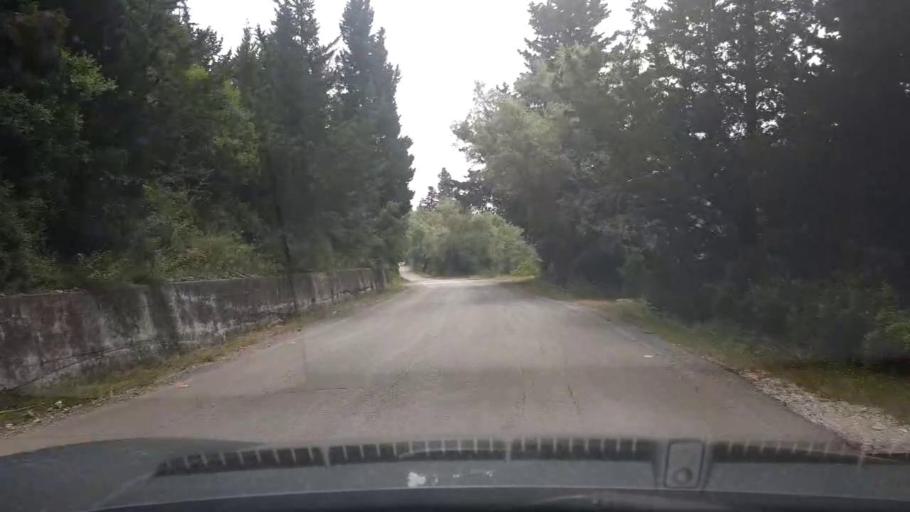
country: GR
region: Ionian Islands
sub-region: Lefkada
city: Nidri
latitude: 38.6483
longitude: 20.7036
